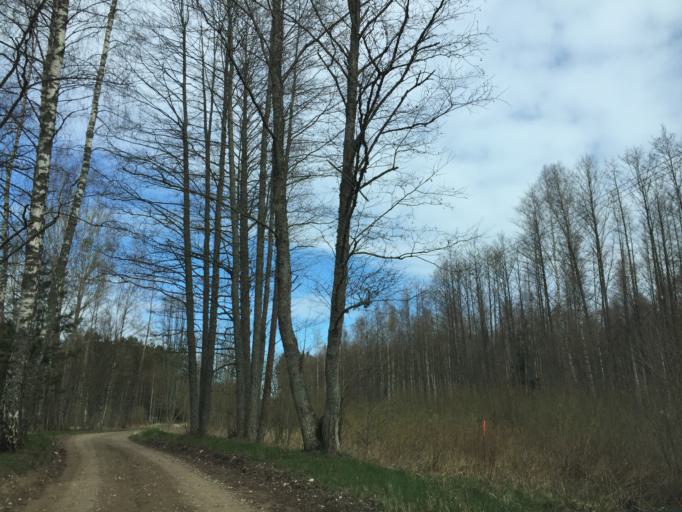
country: LV
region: Salacgrivas
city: Salacgriva
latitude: 57.5345
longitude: 24.3738
